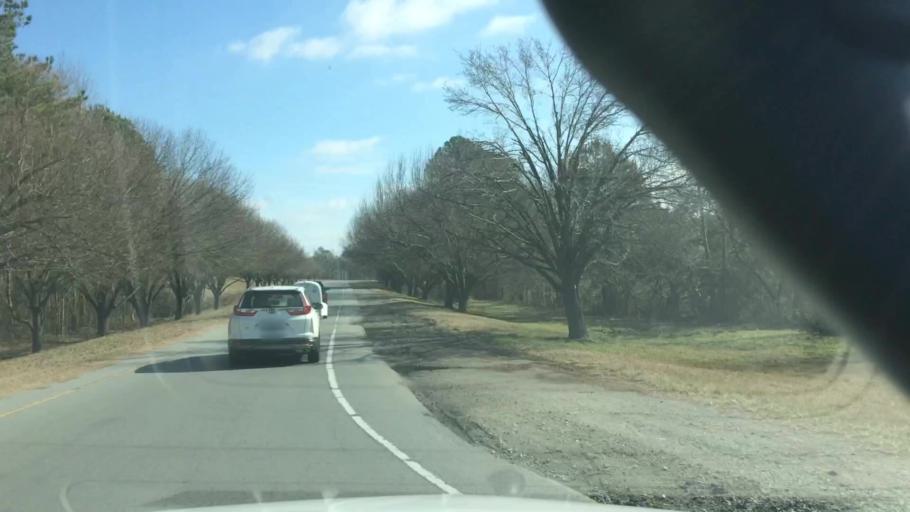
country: US
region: North Carolina
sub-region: Duplin County
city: Wallace
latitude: 34.7540
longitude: -77.9511
